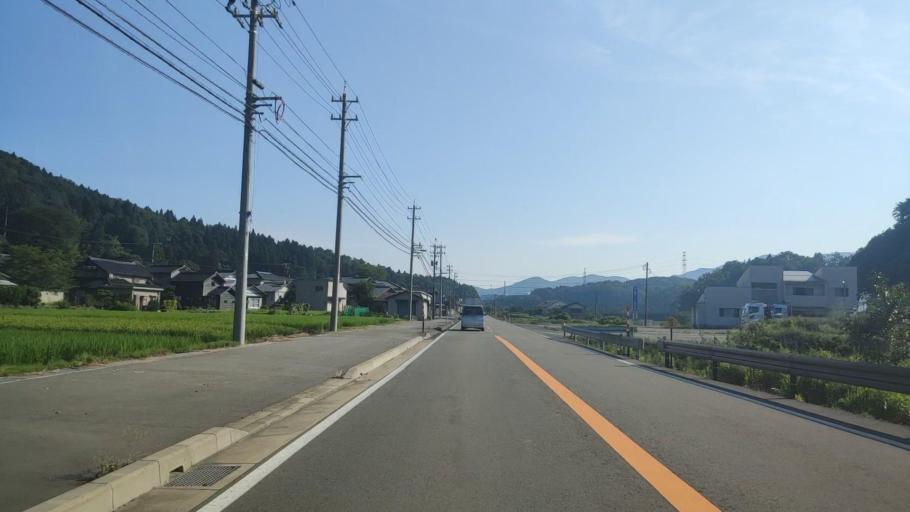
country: JP
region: Fukui
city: Maruoka
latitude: 36.2152
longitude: 136.2728
